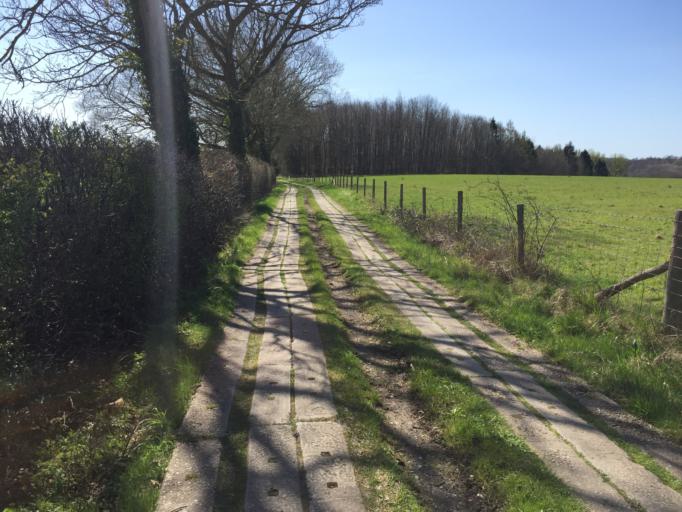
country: GB
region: England
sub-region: East Sussex
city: Wadhurst
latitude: 51.0280
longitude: 0.2906
